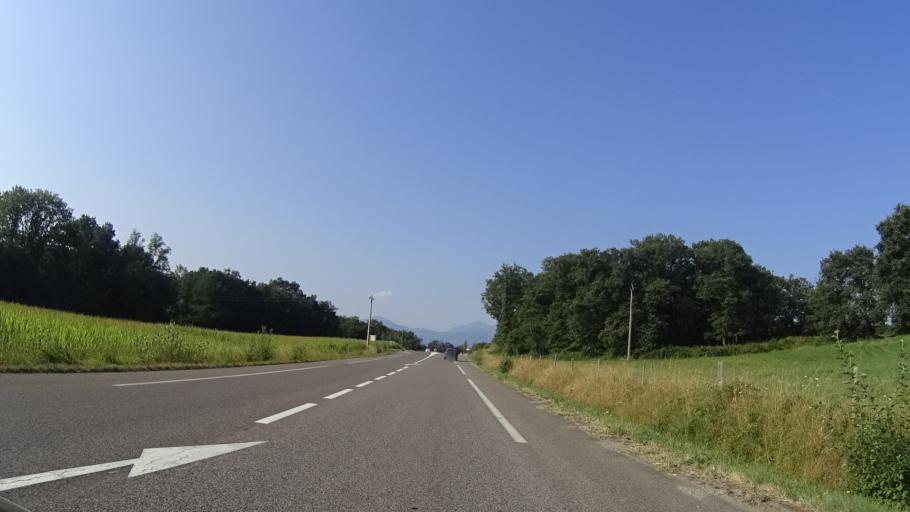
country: FR
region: Midi-Pyrenees
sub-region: Departement de l'Ariege
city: Mirepoix
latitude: 43.0183
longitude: 1.8915
